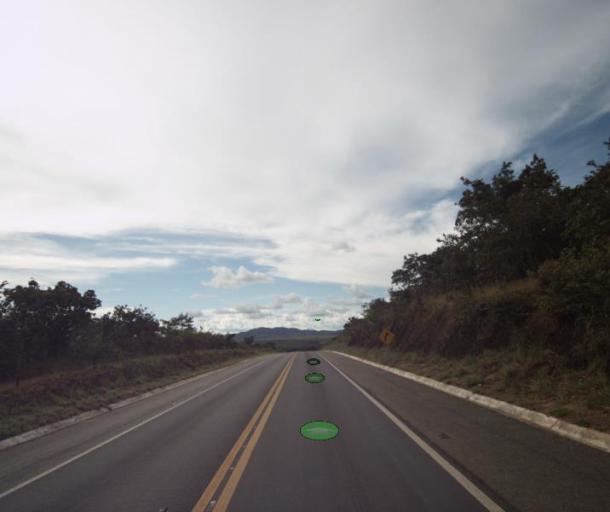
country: BR
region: Goias
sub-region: Barro Alto
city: Barro Alto
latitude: -15.1971
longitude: -48.7029
